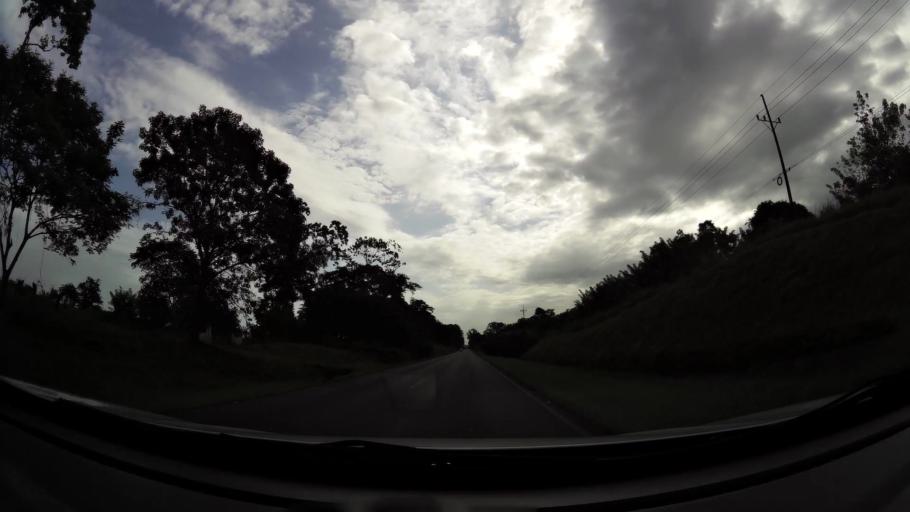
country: CR
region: Limon
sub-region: Canton de Guacimo
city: Guacimo
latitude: 10.1989
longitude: -83.6652
